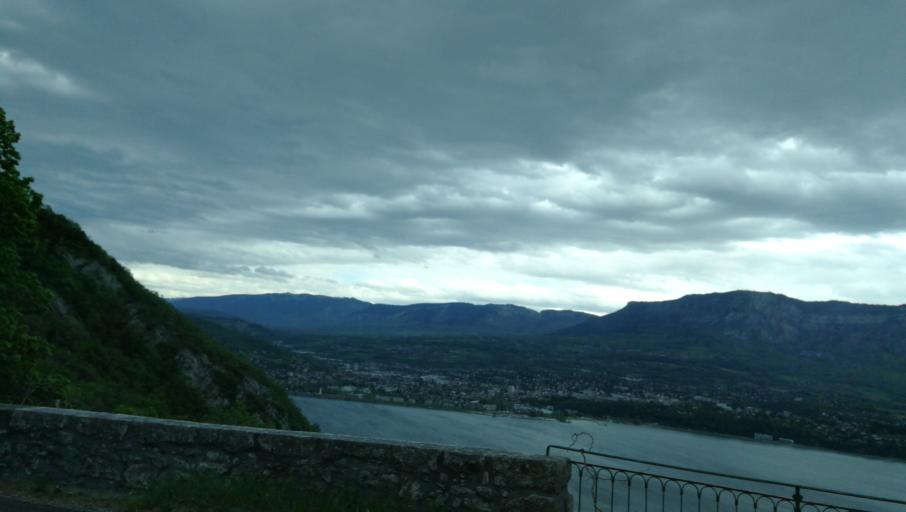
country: FR
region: Rhone-Alpes
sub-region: Departement de la Savoie
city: Le Bourget-du-Lac
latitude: 45.6865
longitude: 5.8524
